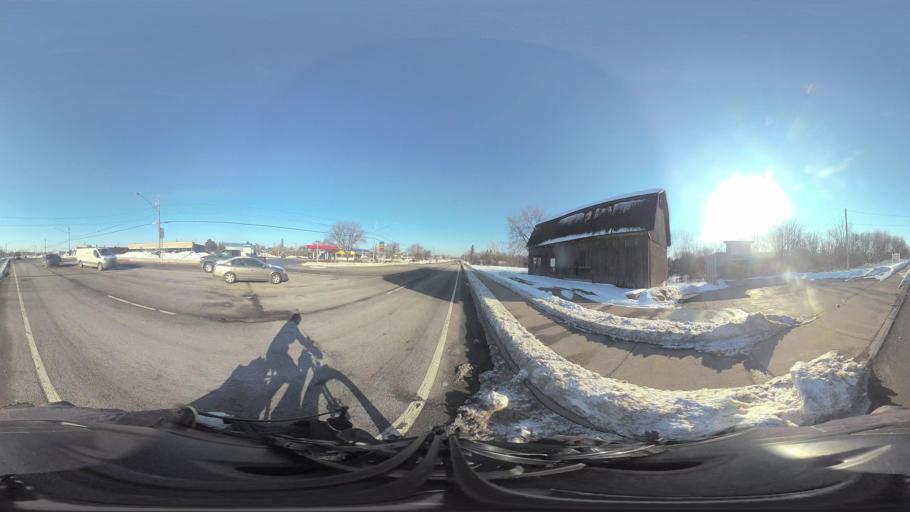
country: US
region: New York
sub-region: Monroe County
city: Rochester
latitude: 43.0711
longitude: -77.6073
